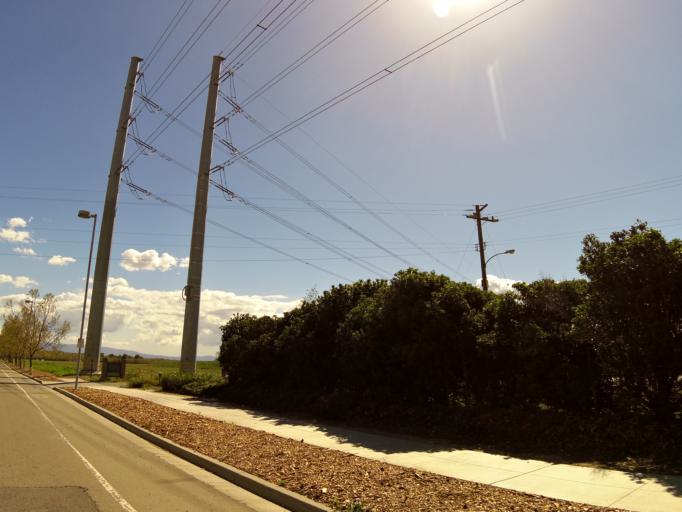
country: US
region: California
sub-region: Santa Clara County
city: Milpitas
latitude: 37.4476
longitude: -121.9223
